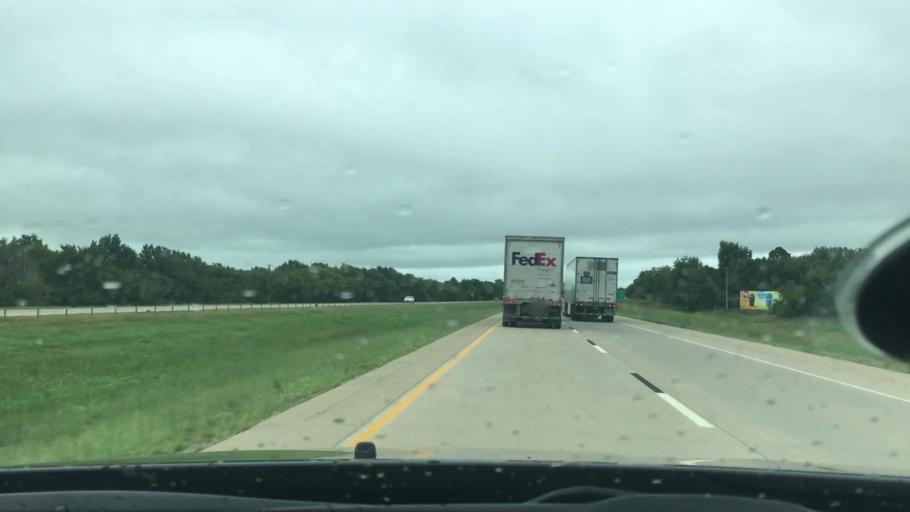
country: US
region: Oklahoma
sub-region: McIntosh County
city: Checotah
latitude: 35.4580
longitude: -95.6305
